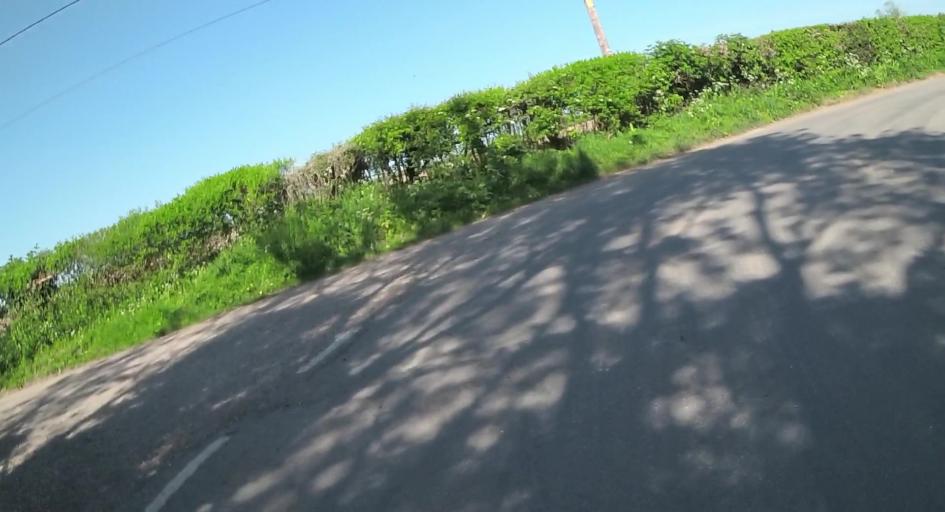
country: GB
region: England
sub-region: Hampshire
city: Kings Worthy
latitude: 51.1511
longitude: -1.2909
